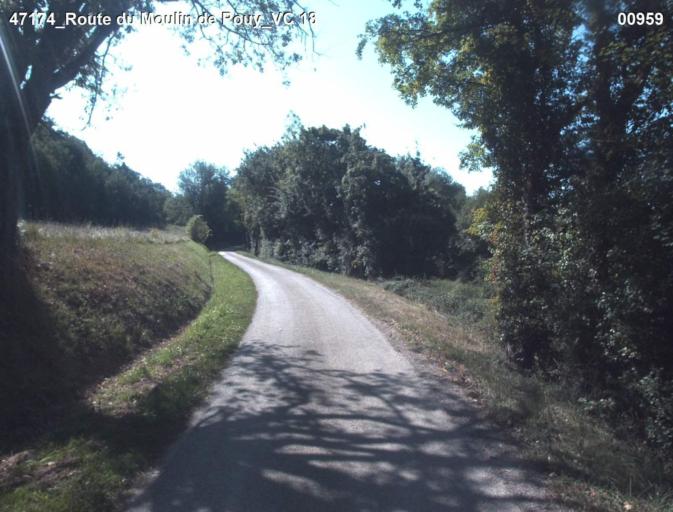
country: FR
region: Aquitaine
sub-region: Departement du Lot-et-Garonne
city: Mezin
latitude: 44.0557
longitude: 0.3183
